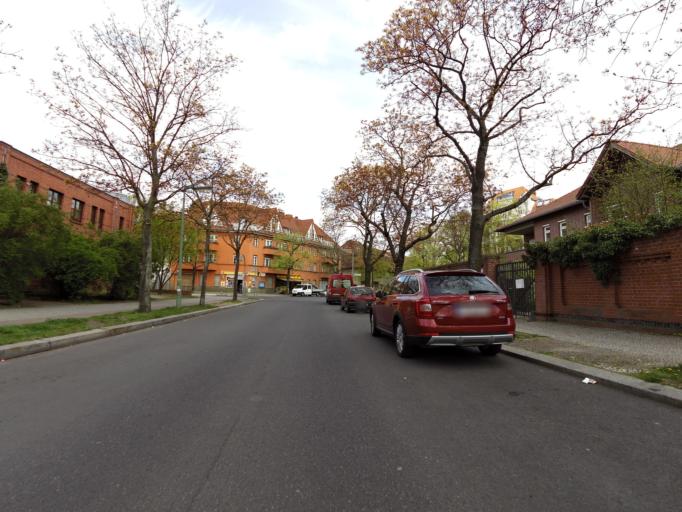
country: DE
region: Berlin
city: Britz
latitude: 52.4545
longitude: 13.4444
